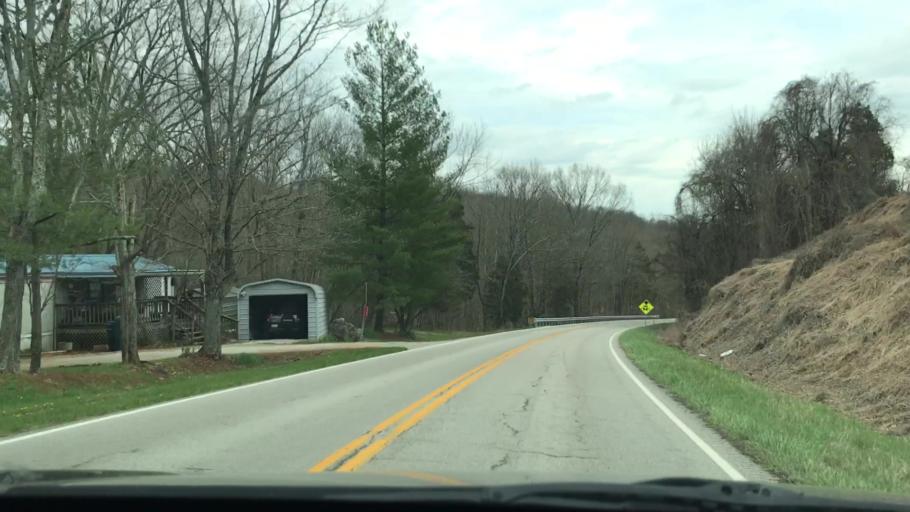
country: US
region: Kentucky
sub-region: Hart County
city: Munfordville
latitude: 37.3266
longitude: -85.7634
